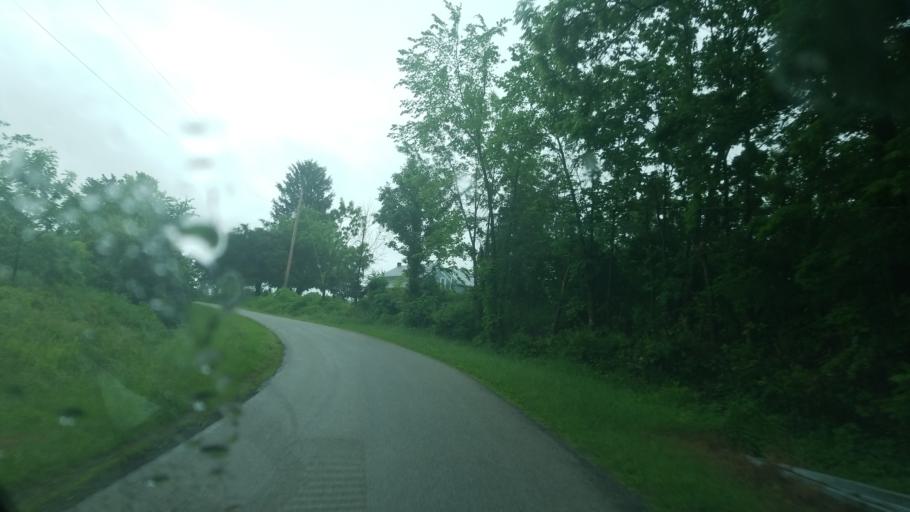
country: US
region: Ohio
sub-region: Huron County
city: Willard
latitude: 40.9432
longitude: -82.7839
